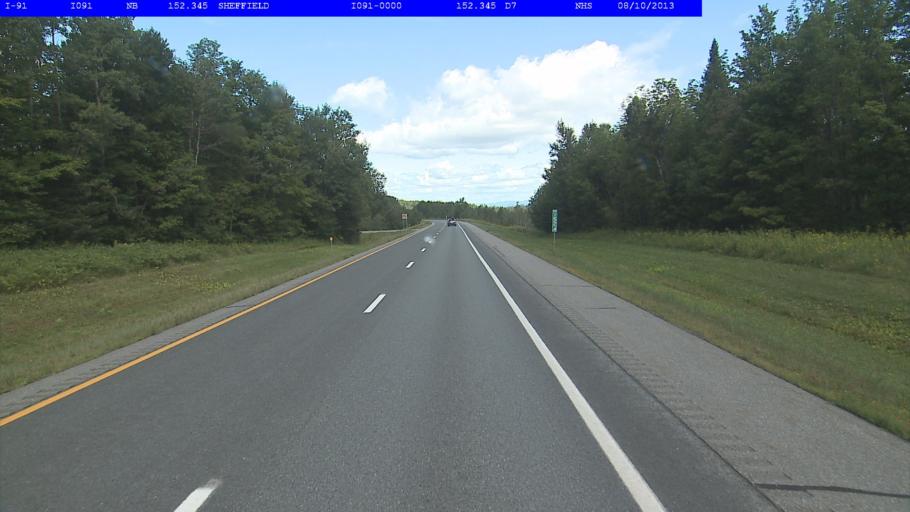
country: US
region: Vermont
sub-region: Caledonia County
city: Lyndonville
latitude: 44.6970
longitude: -72.1419
